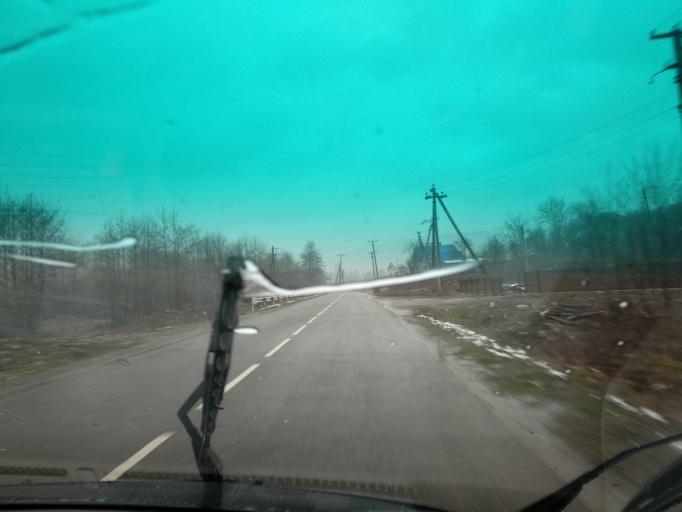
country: RU
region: Krasnodarskiy
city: Khadyzhensk
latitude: 44.2438
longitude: 39.3765
